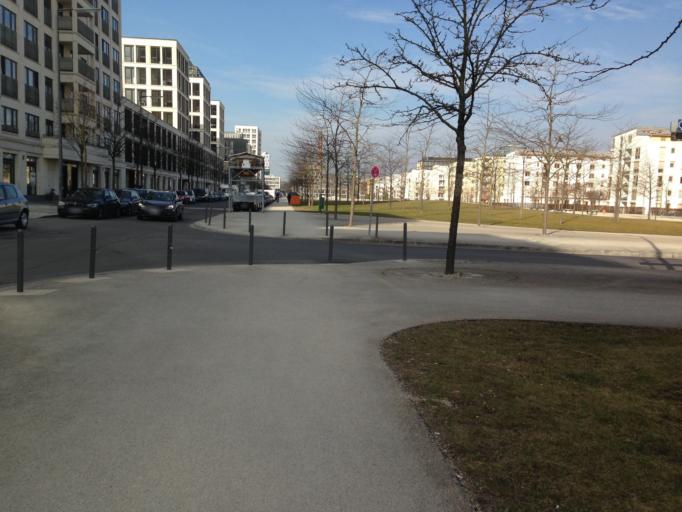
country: DE
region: Bavaria
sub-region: Upper Bavaria
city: Munich
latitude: 48.1429
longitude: 11.5450
